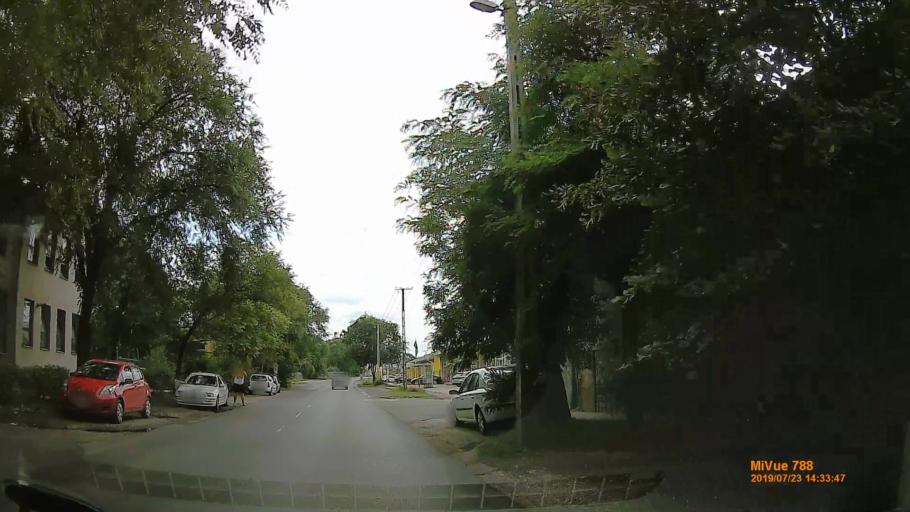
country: HU
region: Szabolcs-Szatmar-Bereg
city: Nyiregyhaza
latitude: 47.9403
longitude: 21.7130
